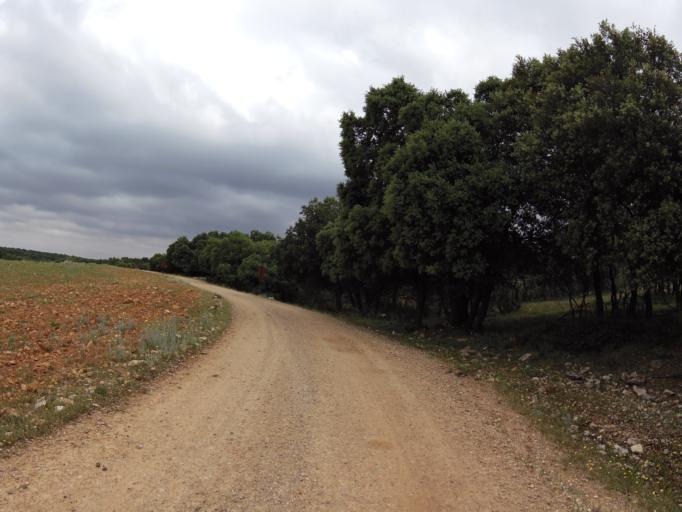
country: ES
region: Castille-La Mancha
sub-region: Provincia de Albacete
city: Robledo
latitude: 38.7444
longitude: -2.4694
